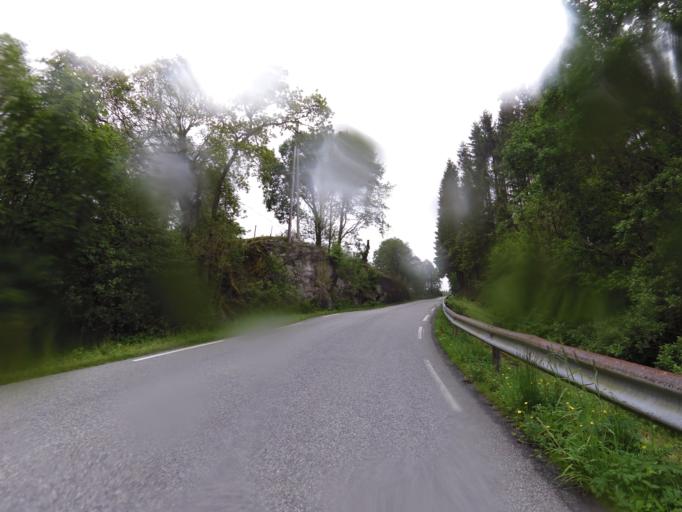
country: NO
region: Hordaland
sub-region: Sveio
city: Sveio
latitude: 59.5272
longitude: 5.2799
